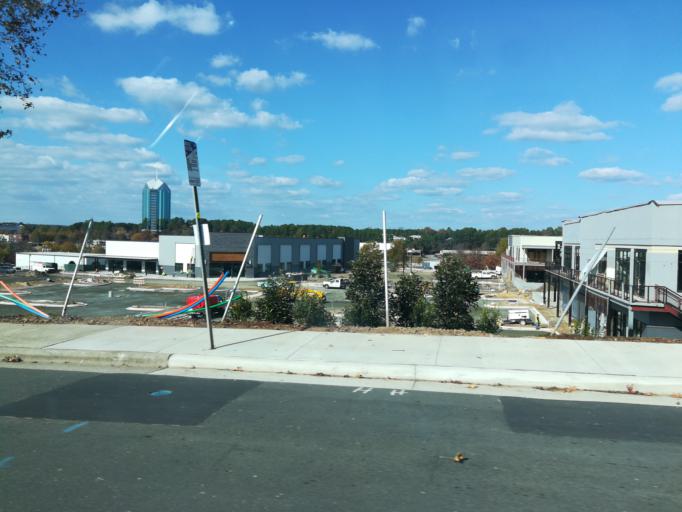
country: US
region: North Carolina
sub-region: Durham County
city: Durham
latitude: 35.9664
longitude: -78.9528
